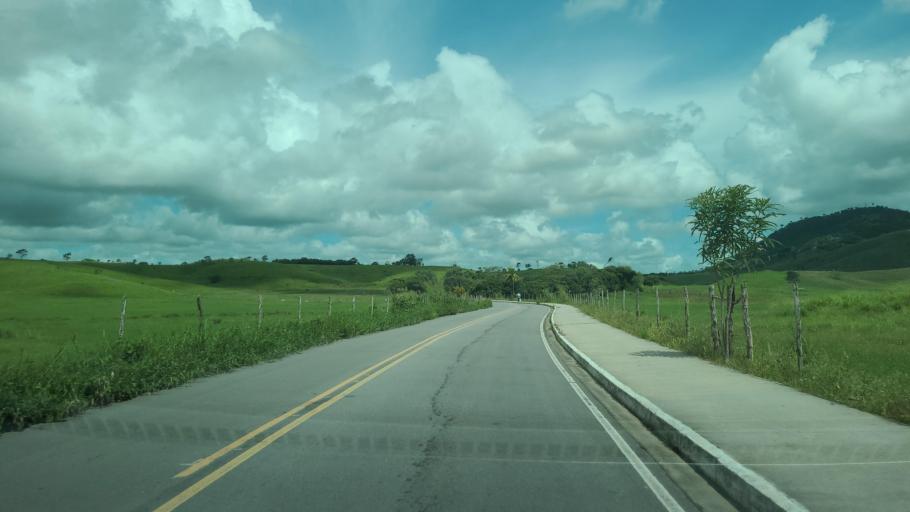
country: BR
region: Alagoas
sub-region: Uniao Dos Palmares
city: Uniao dos Palmares
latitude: -9.1611
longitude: -36.0469
